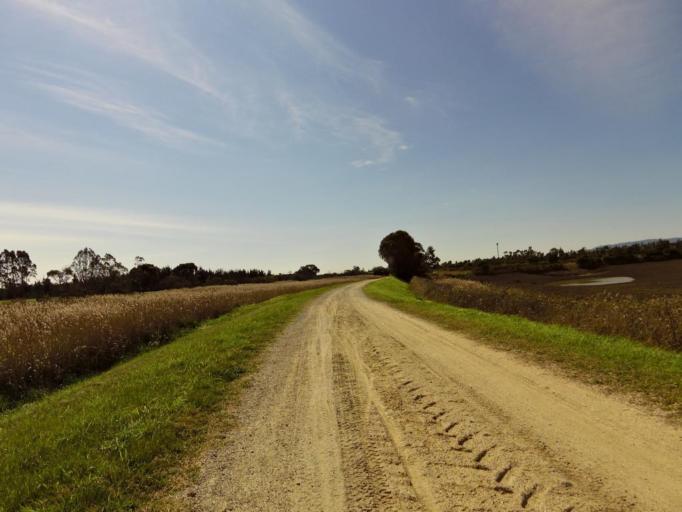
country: AU
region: Victoria
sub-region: Greater Dandenong
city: Keysborough
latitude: -38.0277
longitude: 145.1864
